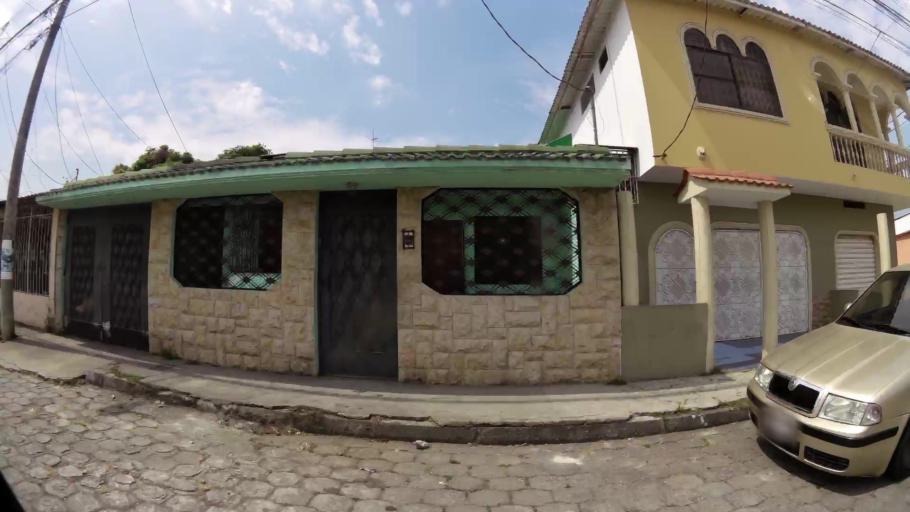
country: EC
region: Guayas
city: Eloy Alfaro
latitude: -2.1222
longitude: -79.9038
